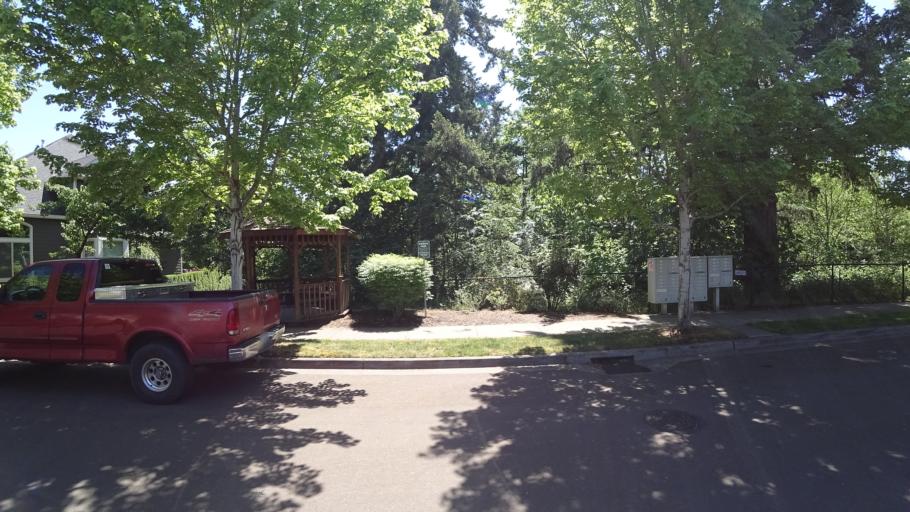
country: US
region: Oregon
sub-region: Washington County
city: Rockcreek
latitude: 45.5252
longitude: -122.9140
